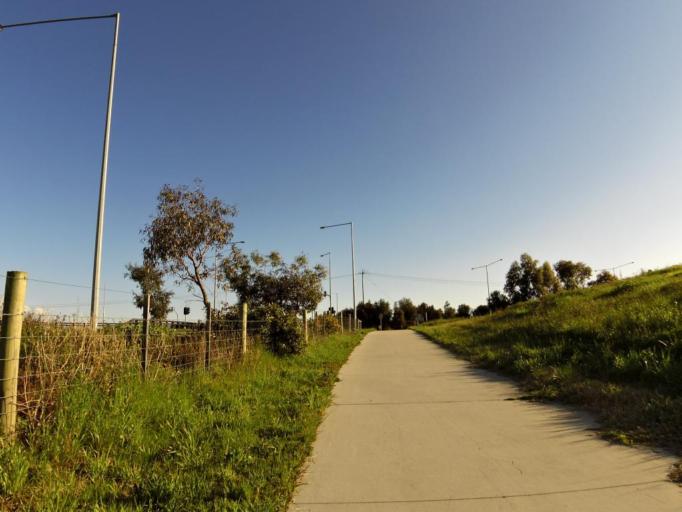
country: AU
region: Victoria
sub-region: Monash
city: Mulgrave
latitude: -37.9245
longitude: 145.2126
